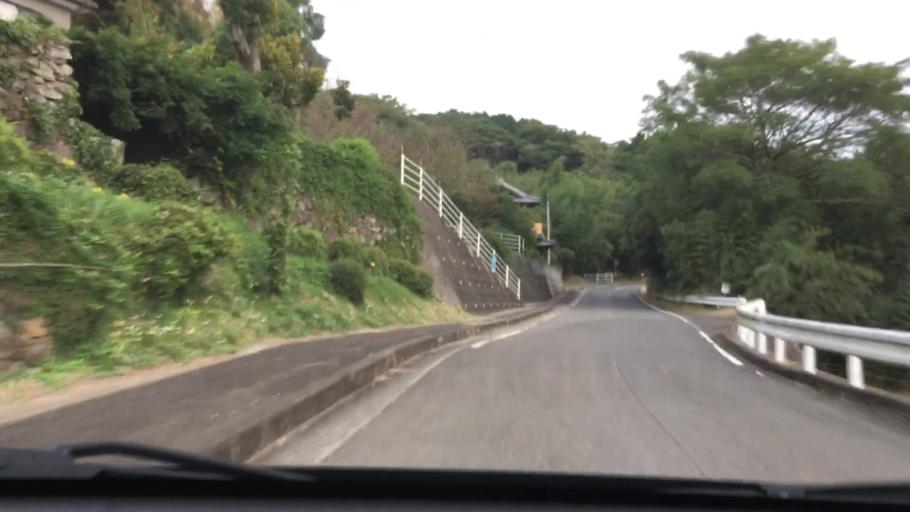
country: JP
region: Nagasaki
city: Sasebo
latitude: 33.0047
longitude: 129.7633
